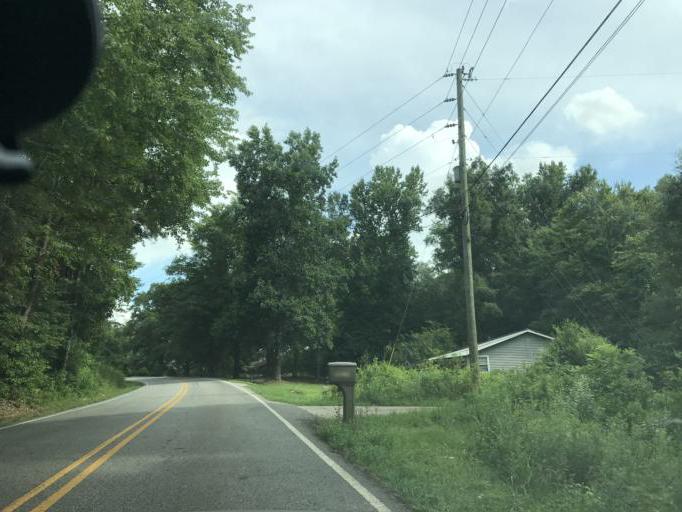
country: US
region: Georgia
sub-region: Forsyth County
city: Cumming
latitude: 34.3017
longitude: -84.1560
